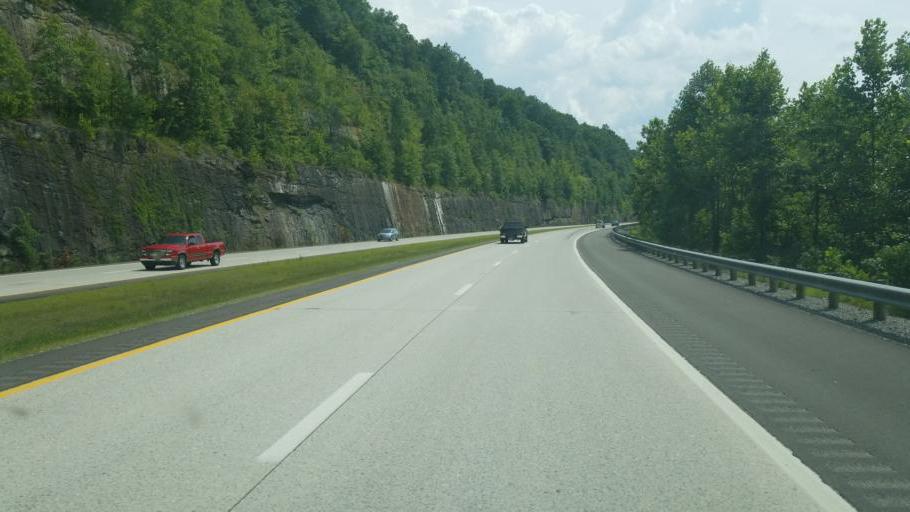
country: US
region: West Virginia
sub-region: Kanawha County
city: Alum Creek
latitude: 38.1930
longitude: -81.8458
